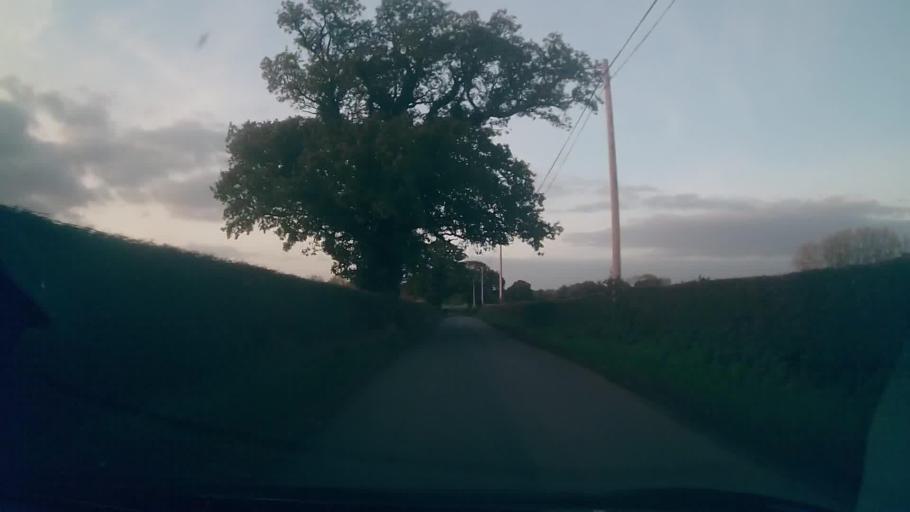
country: GB
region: England
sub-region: Shropshire
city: Clive
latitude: 52.8266
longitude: -2.7294
